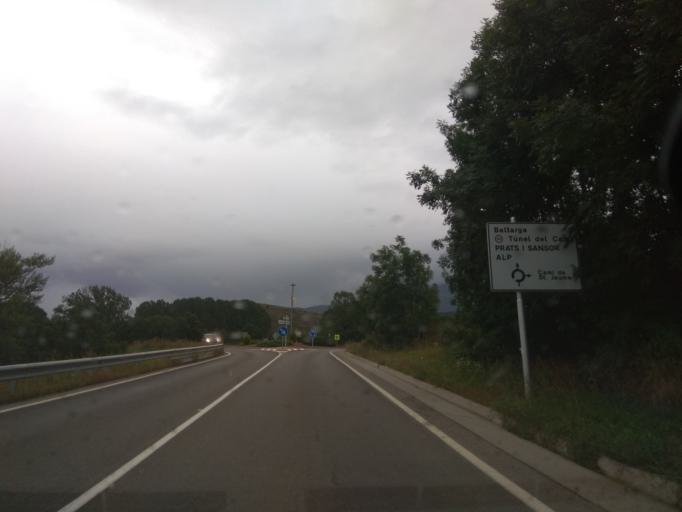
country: ES
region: Catalonia
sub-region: Provincia de Lleida
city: Bellver de Cerdanya
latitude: 42.3685
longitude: 1.7893
